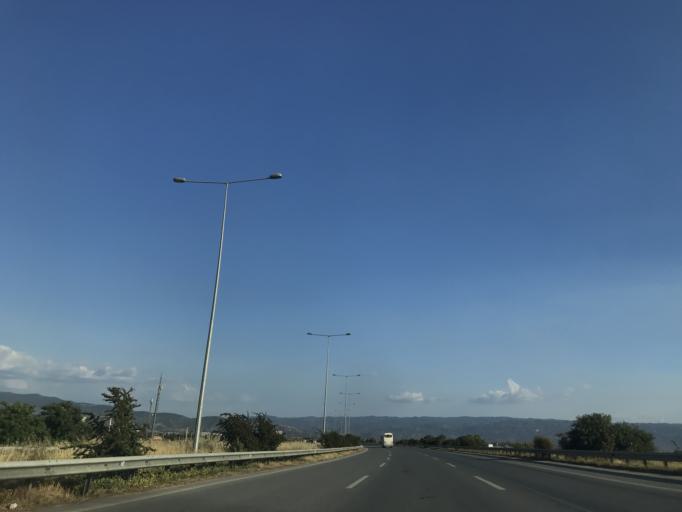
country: TR
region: Aydin
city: Aydin
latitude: 37.8319
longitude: 27.8101
